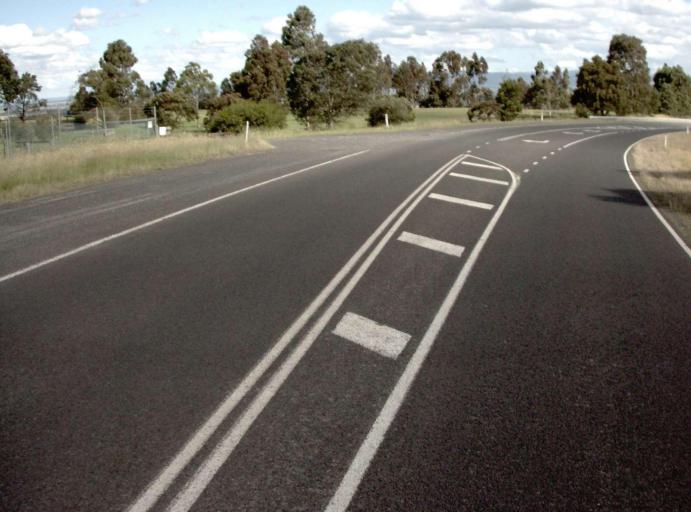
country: AU
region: Victoria
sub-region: Latrobe
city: Moe
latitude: -38.1878
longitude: 146.3294
